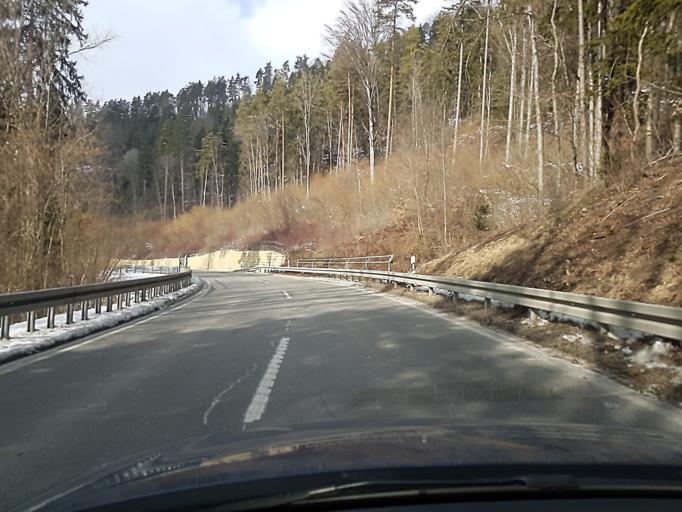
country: DE
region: Baden-Wuerttemberg
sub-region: Freiburg Region
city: Muhlheim am Bach
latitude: 48.3976
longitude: 8.6653
